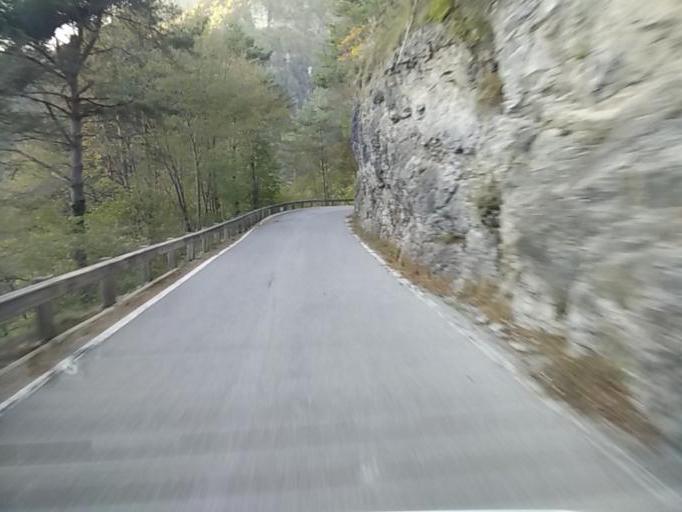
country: IT
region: Lombardy
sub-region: Provincia di Brescia
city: Valvestino
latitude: 45.7128
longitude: 10.6119
